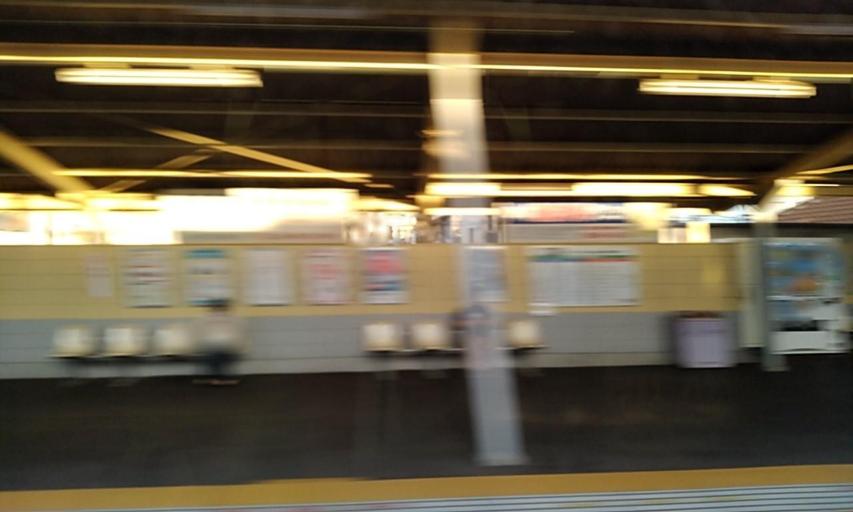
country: JP
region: Osaka
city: Sakai
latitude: 34.6062
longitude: 135.4969
